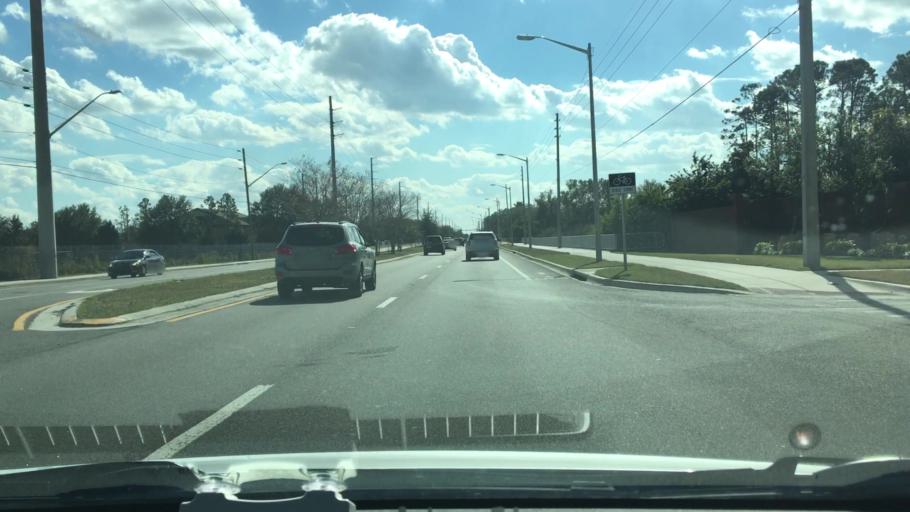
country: US
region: Florida
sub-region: Orange County
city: Conway
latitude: 28.4782
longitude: -81.3309
